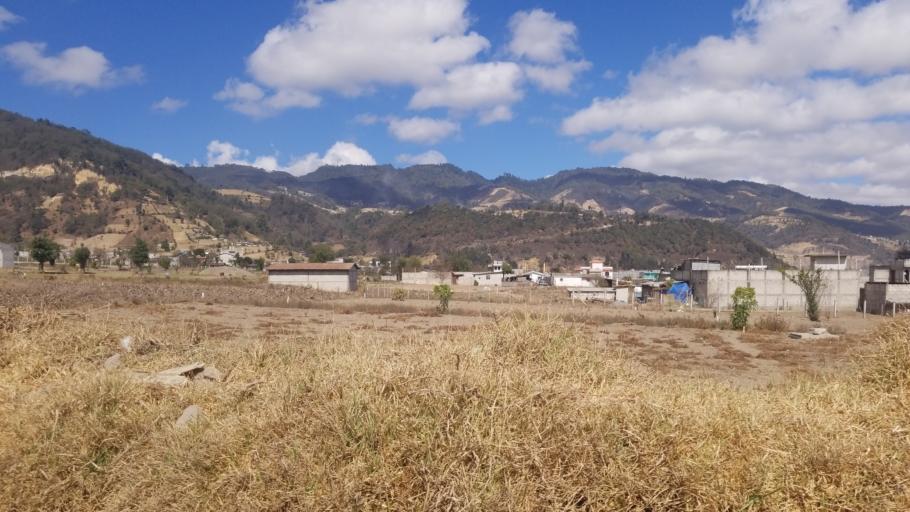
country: GT
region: Quetzaltenango
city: Almolonga
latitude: 14.7897
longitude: -91.5435
